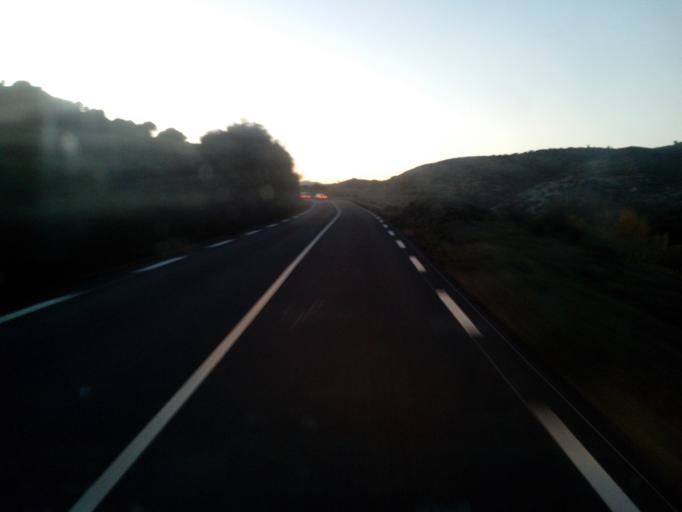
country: FR
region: Languedoc-Roussillon
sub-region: Departement des Pyrenees-Orientales
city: Estagel
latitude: 42.7762
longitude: 2.7333
